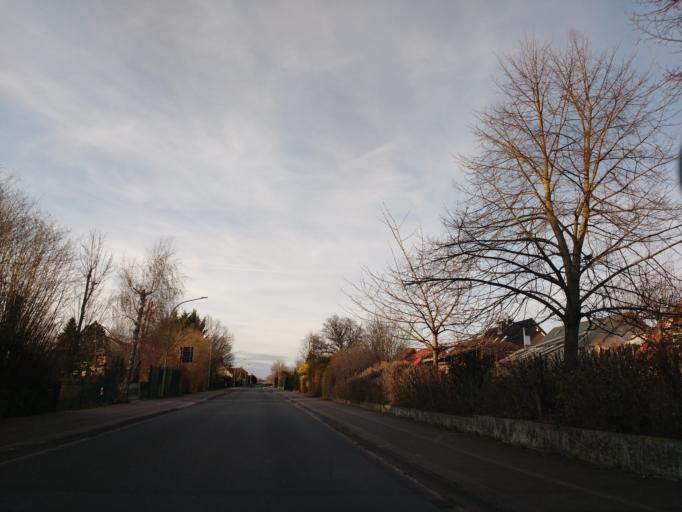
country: DE
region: North Rhine-Westphalia
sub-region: Regierungsbezirk Detmold
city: Salzkotten
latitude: 51.6672
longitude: 8.6156
